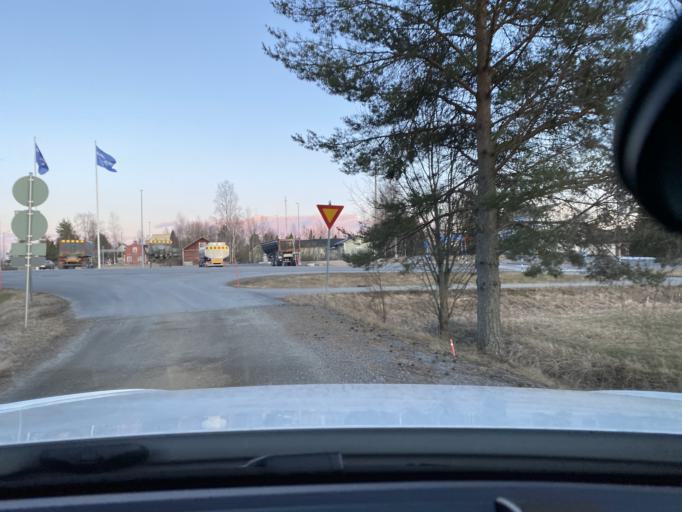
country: FI
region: Pirkanmaa
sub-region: Lounais-Pirkanmaa
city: Punkalaidun
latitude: 61.1181
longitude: 23.0848
